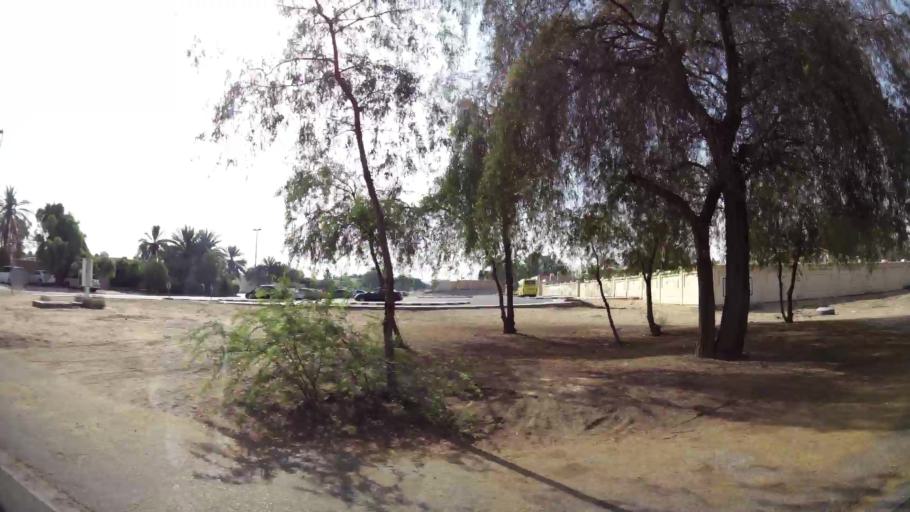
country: AE
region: Ash Shariqah
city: Sharjah
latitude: 25.2222
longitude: 55.3976
